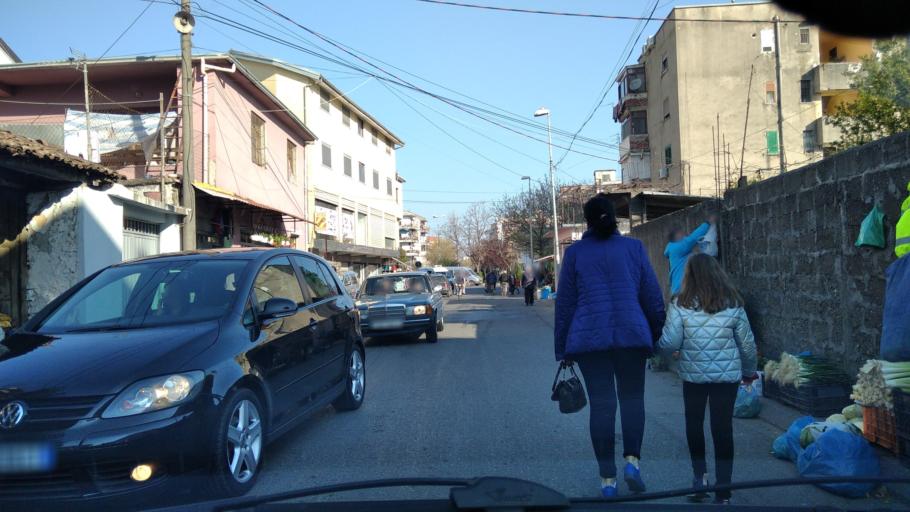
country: AL
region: Shkoder
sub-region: Rrethi i Shkodres
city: Shkoder
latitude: 42.0604
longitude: 19.5132
